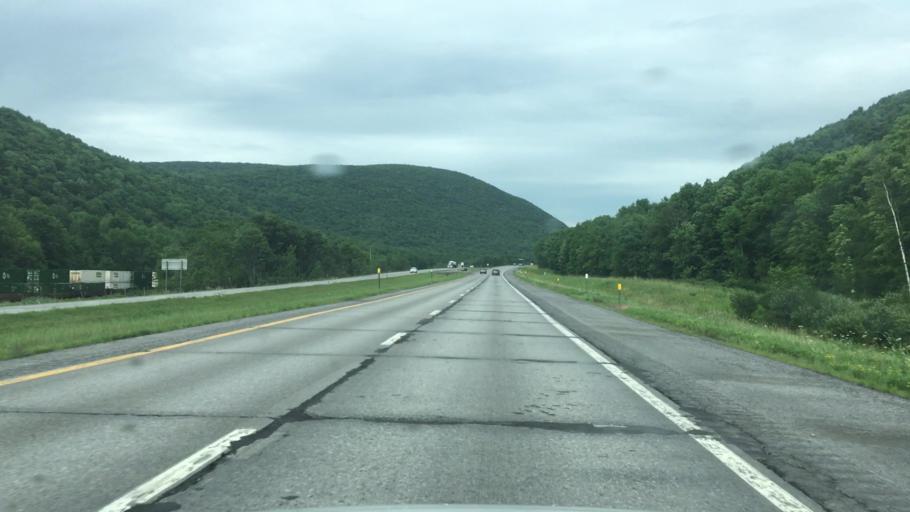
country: US
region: New York
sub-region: Otsego County
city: Worcester
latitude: 42.6381
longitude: -74.6529
